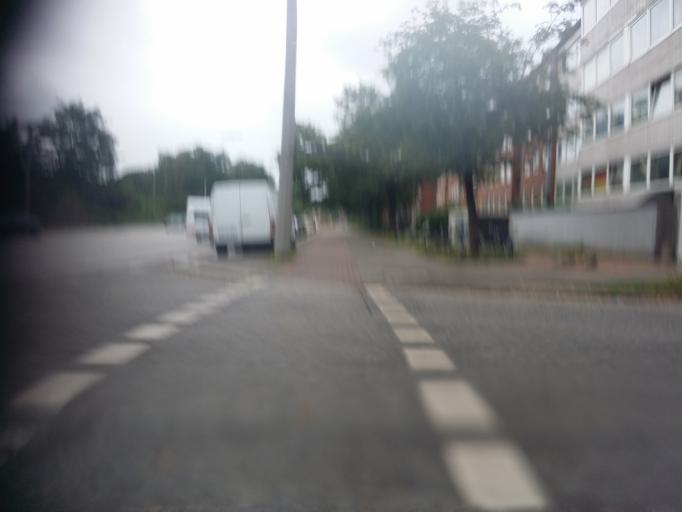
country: DE
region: Hamburg
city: Borgfelde
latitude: 53.5549
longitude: 10.0366
